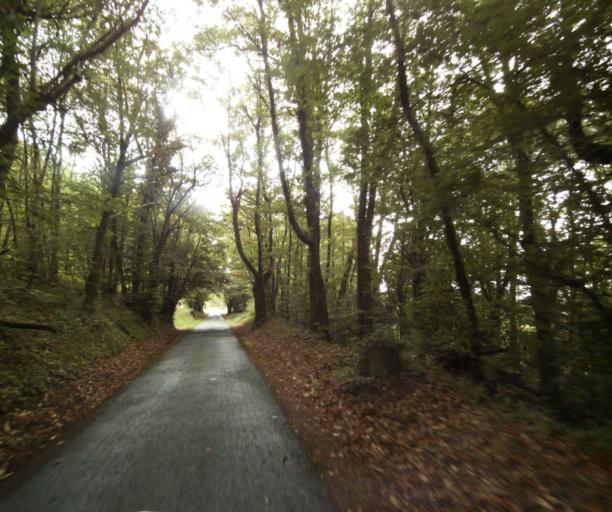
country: FR
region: Limousin
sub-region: Departement de la Correze
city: Sainte-Fortunade
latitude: 45.1903
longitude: 1.8072
